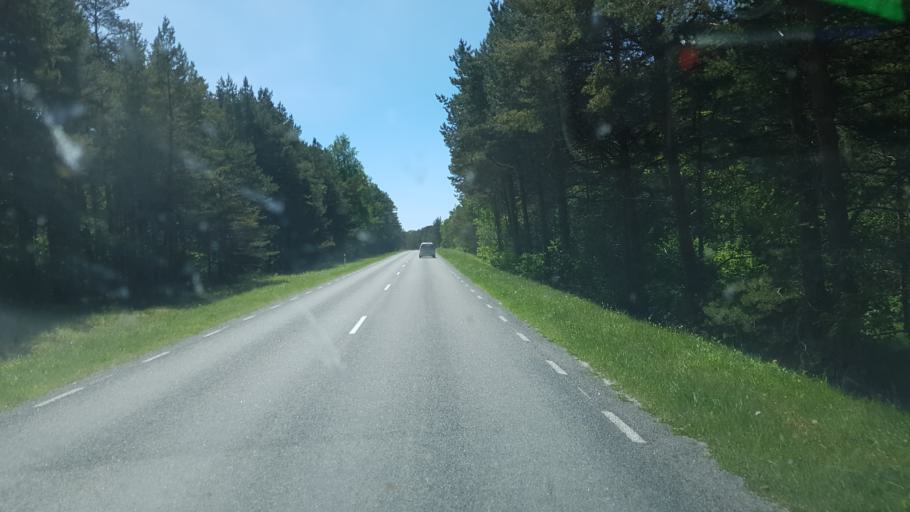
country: EE
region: Saare
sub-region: Kuressaare linn
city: Kuressaare
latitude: 58.1193
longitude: 22.2415
